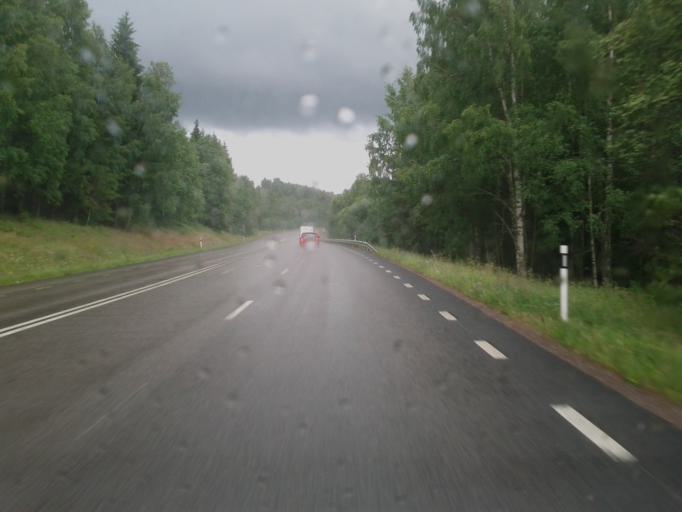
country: SE
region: Dalarna
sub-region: Rattviks Kommun
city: Vikarbyn
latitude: 60.9079
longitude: 15.0607
